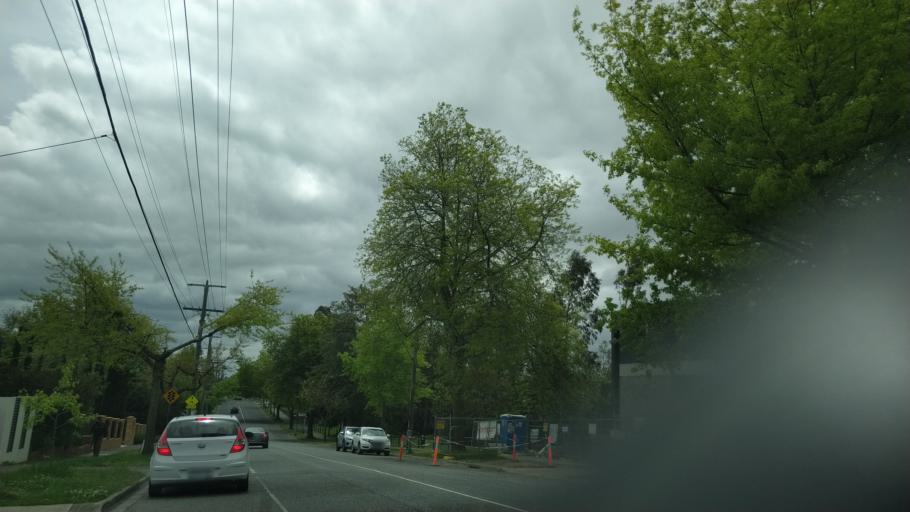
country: AU
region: Victoria
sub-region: Glen Eira
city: Murrumbeena
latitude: -37.8832
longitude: 145.0789
